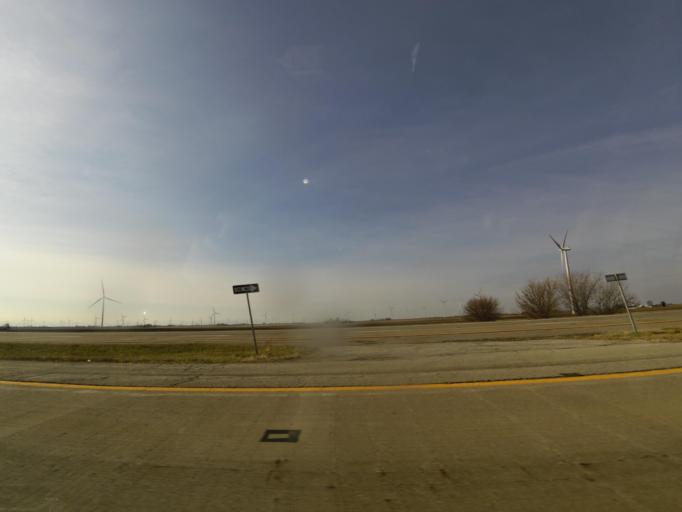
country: US
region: Illinois
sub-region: Macon County
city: Maroa
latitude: 40.0331
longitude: -88.9644
